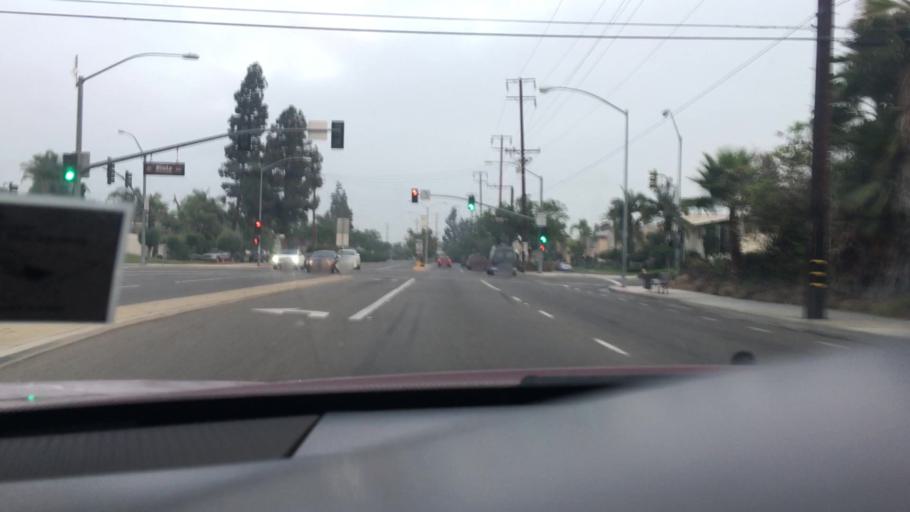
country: US
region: California
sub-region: Los Angeles County
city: La Mirada
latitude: 33.9004
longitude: -118.0187
